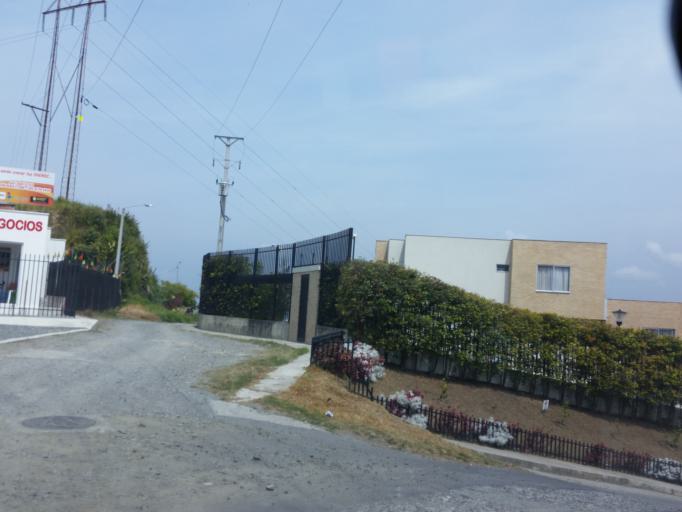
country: CO
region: Caldas
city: Manizales
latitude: 5.0868
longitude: -75.5285
